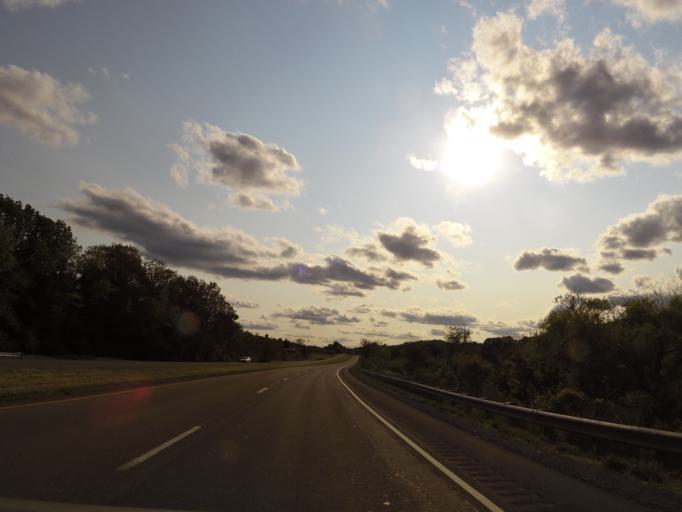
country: US
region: Virginia
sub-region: Tazewell County
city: Tazewell
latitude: 37.1203
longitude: -81.5756
